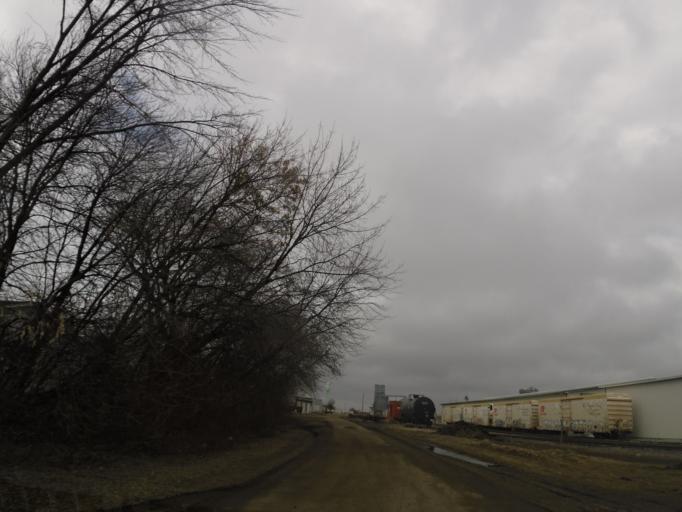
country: US
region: North Dakota
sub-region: Walsh County
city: Grafton
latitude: 48.4145
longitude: -97.4084
